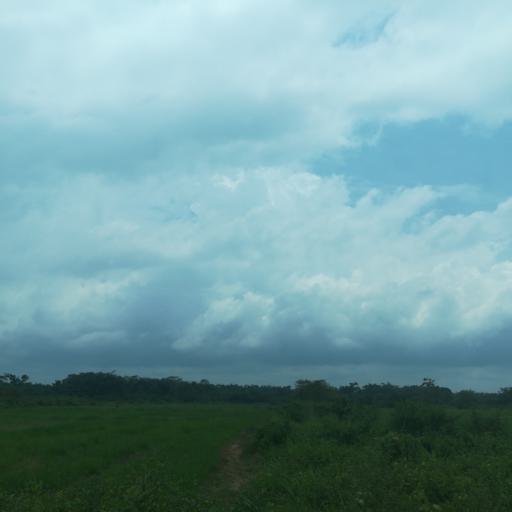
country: NG
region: Lagos
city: Ejirin
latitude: 6.6716
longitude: 3.8016
